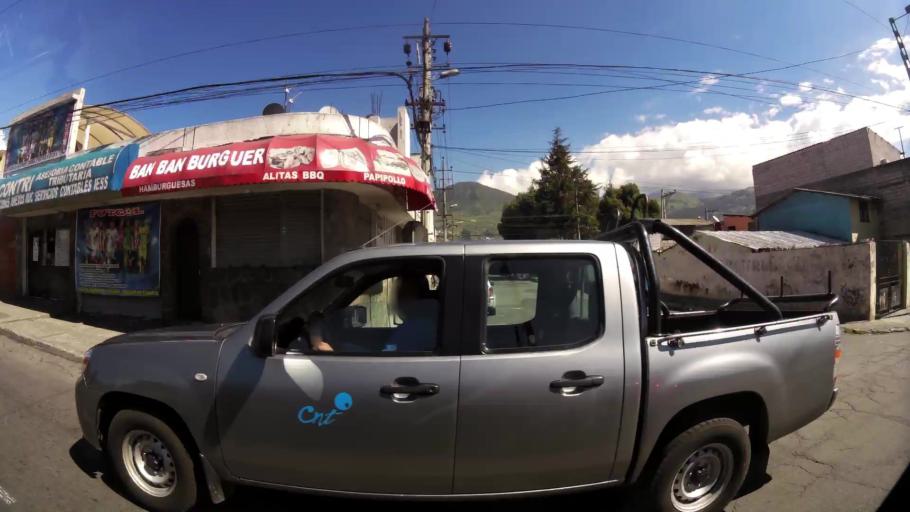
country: EC
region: Pichincha
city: Quito
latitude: -0.2582
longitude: -78.5296
